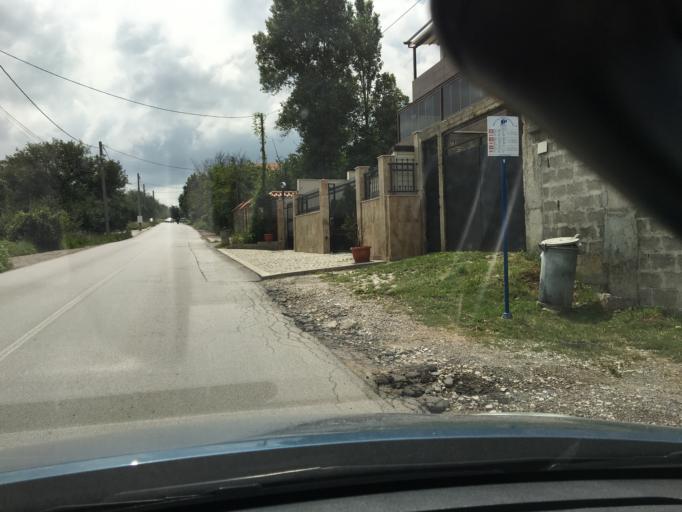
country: BG
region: Sofia-Capital
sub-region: Stolichna Obshtina
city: Sofia
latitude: 42.6056
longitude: 23.3665
